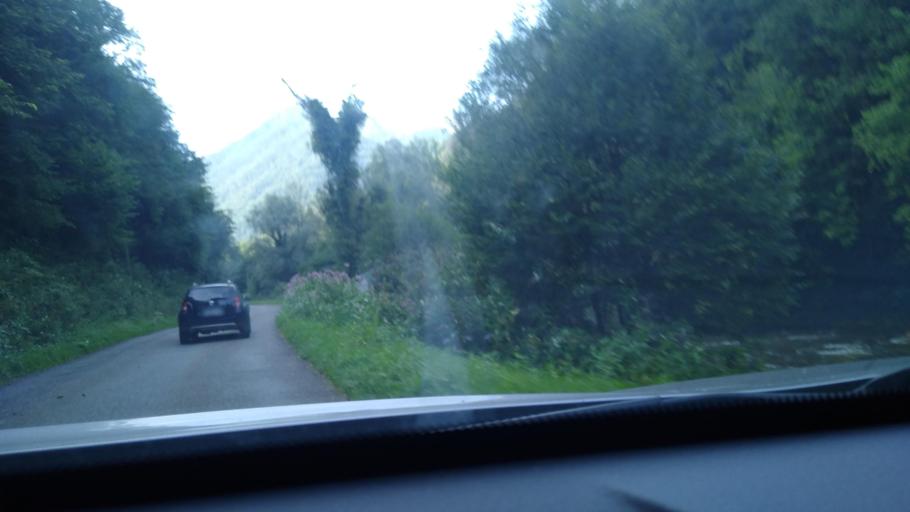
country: FR
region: Midi-Pyrenees
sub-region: Departement de l'Ariege
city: Saint-Girons
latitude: 42.8011
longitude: 1.1929
